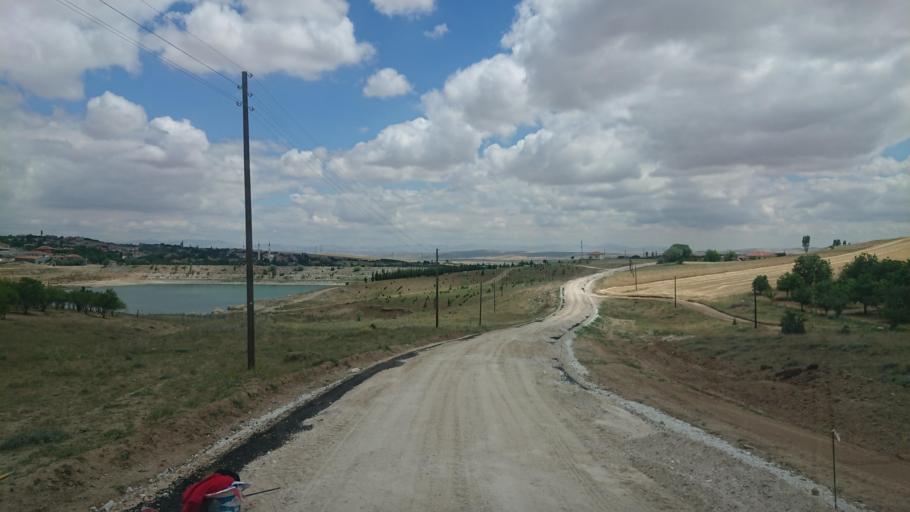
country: TR
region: Aksaray
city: Agacoren
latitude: 38.8610
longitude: 33.9480
